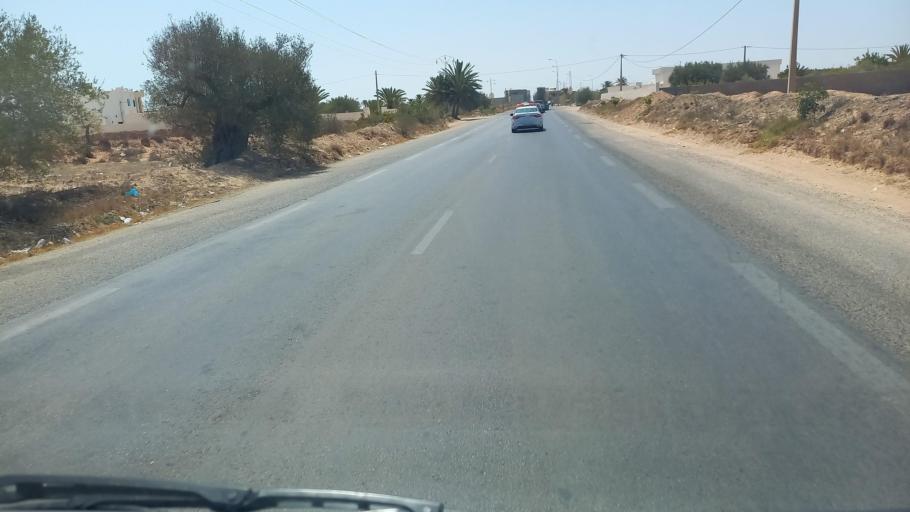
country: TN
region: Madanin
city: Houmt Souk
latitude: 33.7893
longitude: 10.8881
